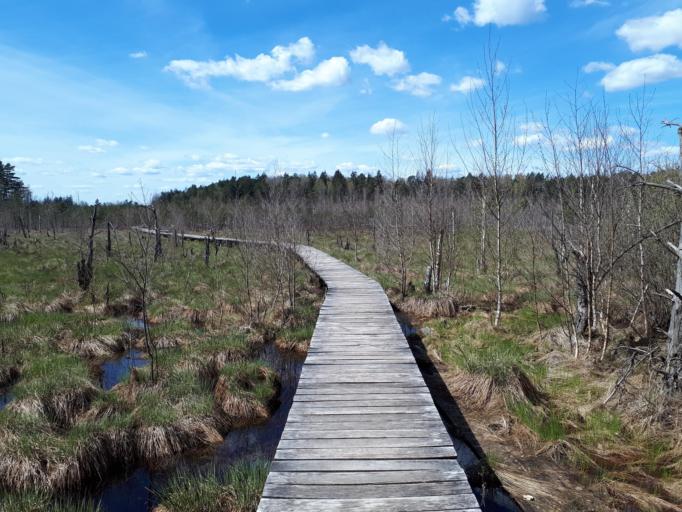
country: LT
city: Ramuciai
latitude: 54.8479
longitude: 24.0785
